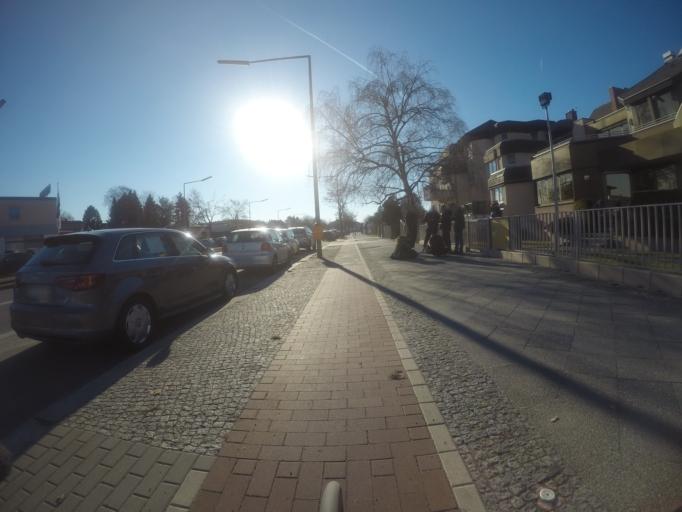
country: DE
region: Berlin
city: Buckow
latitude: 52.4257
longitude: 13.4432
